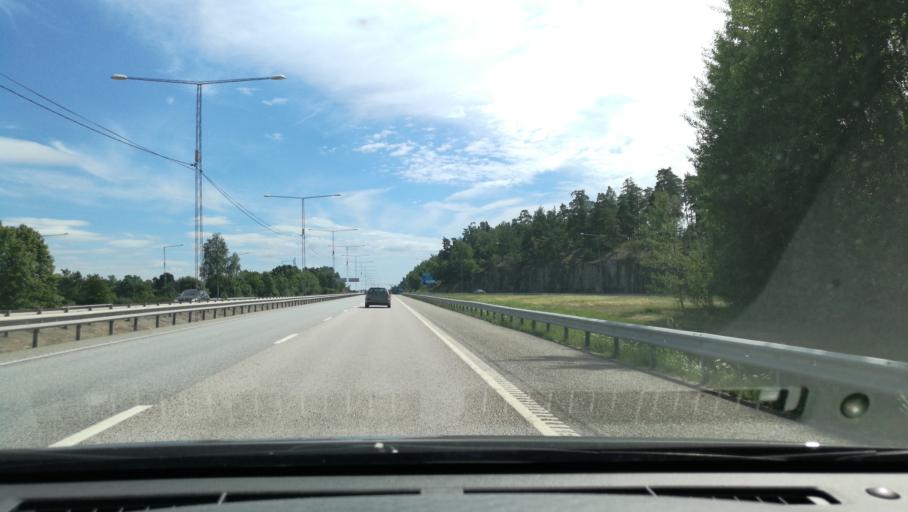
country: SE
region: Stockholm
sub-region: Jarfalla Kommun
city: Jakobsberg
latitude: 59.4210
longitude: 17.8519
